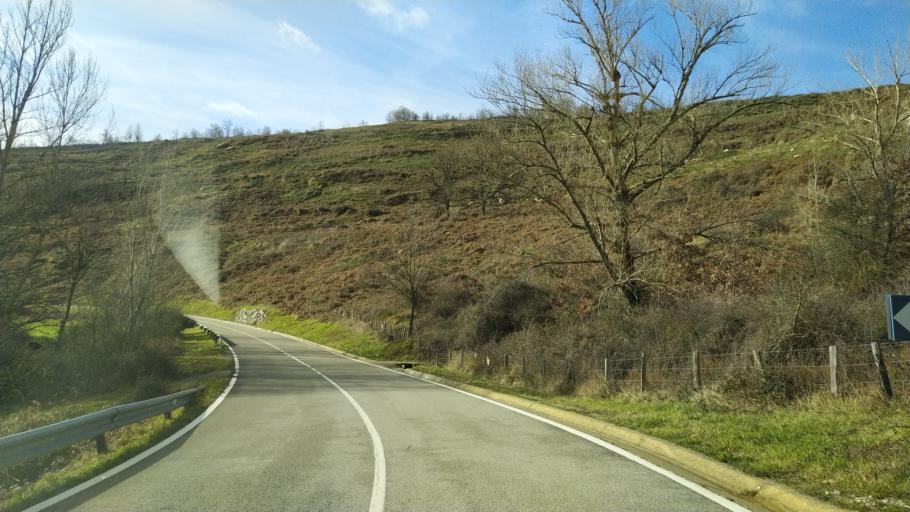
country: ES
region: Cantabria
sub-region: Provincia de Cantabria
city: San Martin de Elines
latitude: 42.8442
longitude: -3.9114
